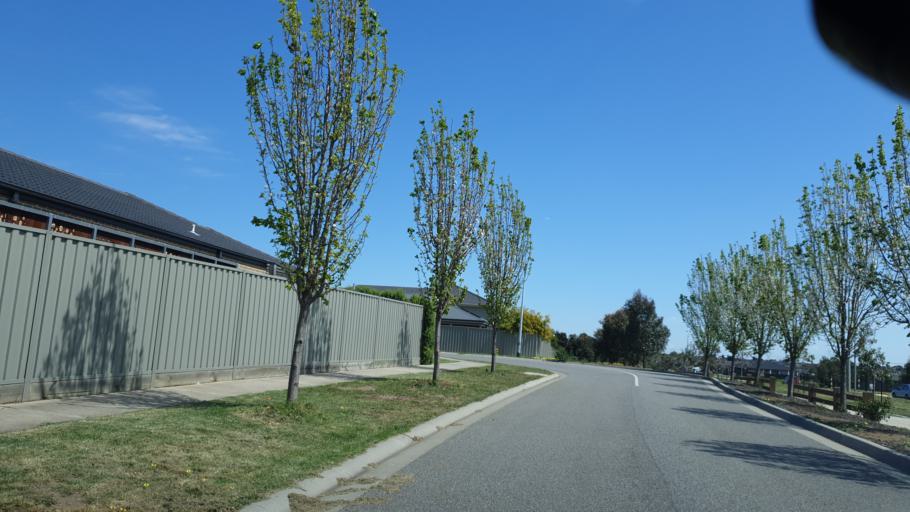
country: AU
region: Victoria
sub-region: Casey
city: Cranbourne East
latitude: -38.1014
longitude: 145.3098
